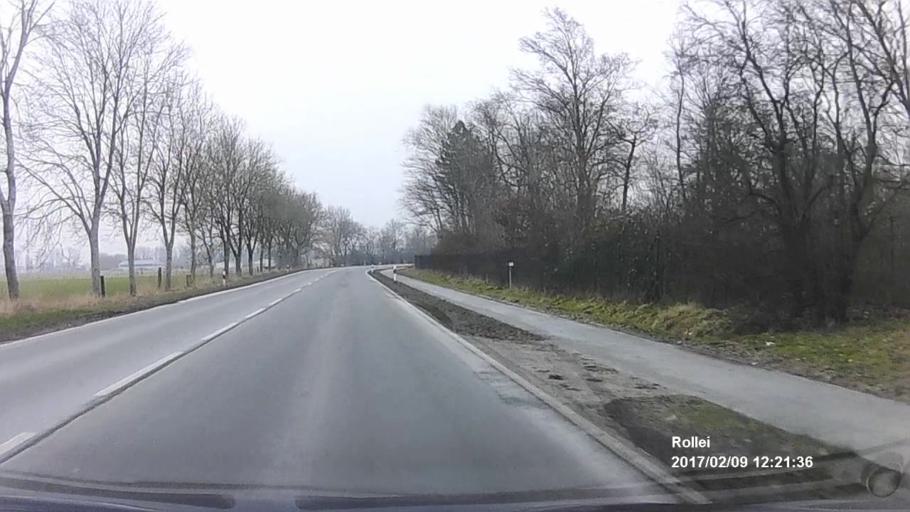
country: DE
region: Lower Saxony
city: Weener
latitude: 53.1688
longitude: 7.3524
